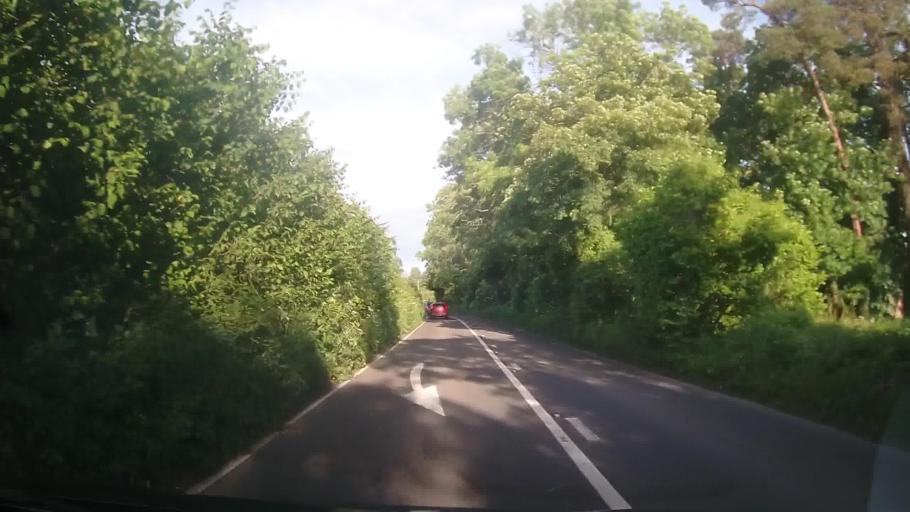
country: GB
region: England
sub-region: Devon
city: Ivybridge
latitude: 50.3520
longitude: -3.9281
